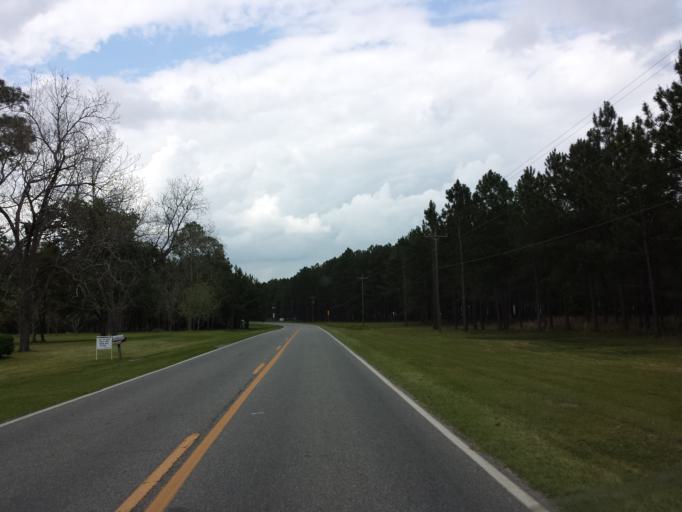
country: US
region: Georgia
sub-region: Cook County
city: Sparks
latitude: 31.2171
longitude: -83.4547
